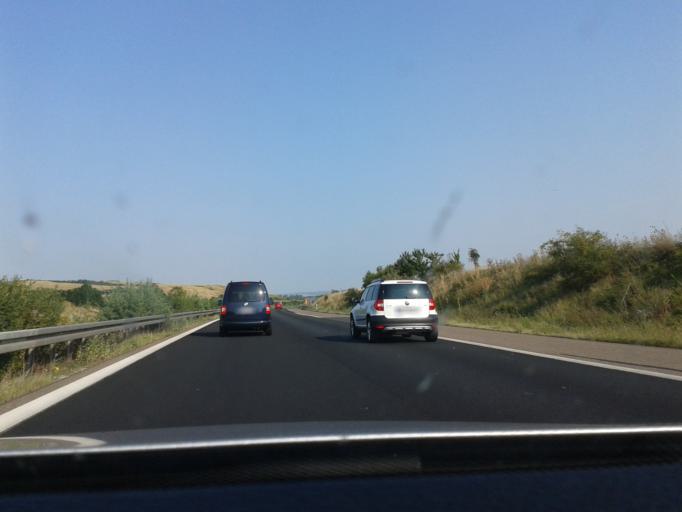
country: DE
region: Saxony-Anhalt
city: Bennungen
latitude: 51.4676
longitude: 11.1216
